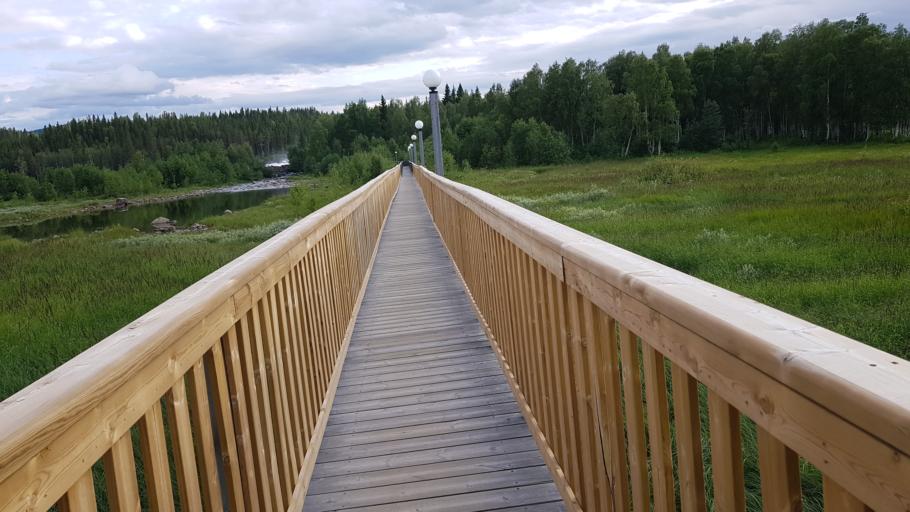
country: SE
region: Norrbotten
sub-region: Alvsbyns Kommun
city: AElvsbyn
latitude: 65.8564
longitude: 20.4173
